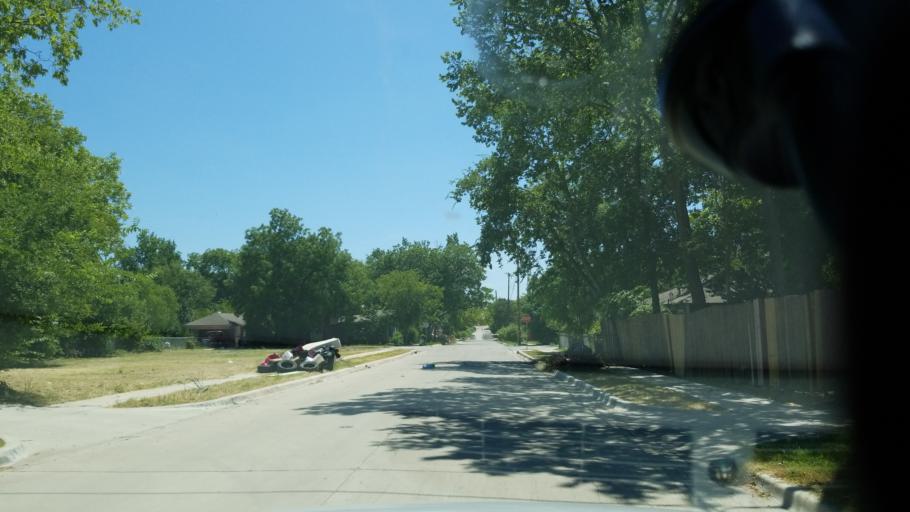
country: US
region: Texas
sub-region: Dallas County
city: Cockrell Hill
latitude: 32.7096
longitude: -96.8189
